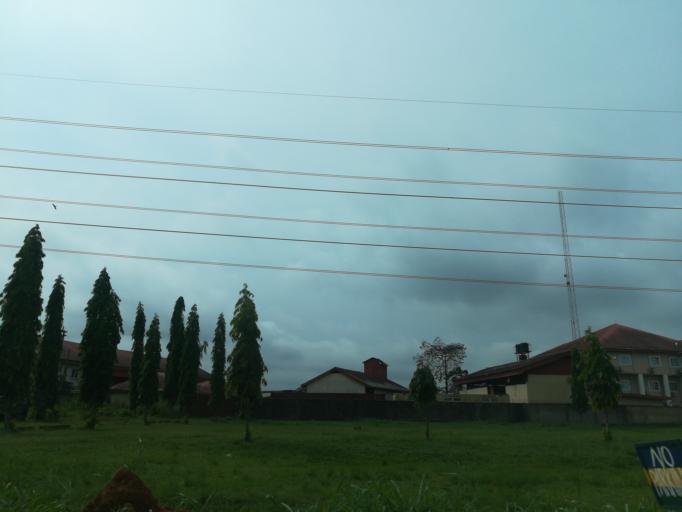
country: NG
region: Rivers
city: Emuoha
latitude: 4.8932
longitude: 6.9727
